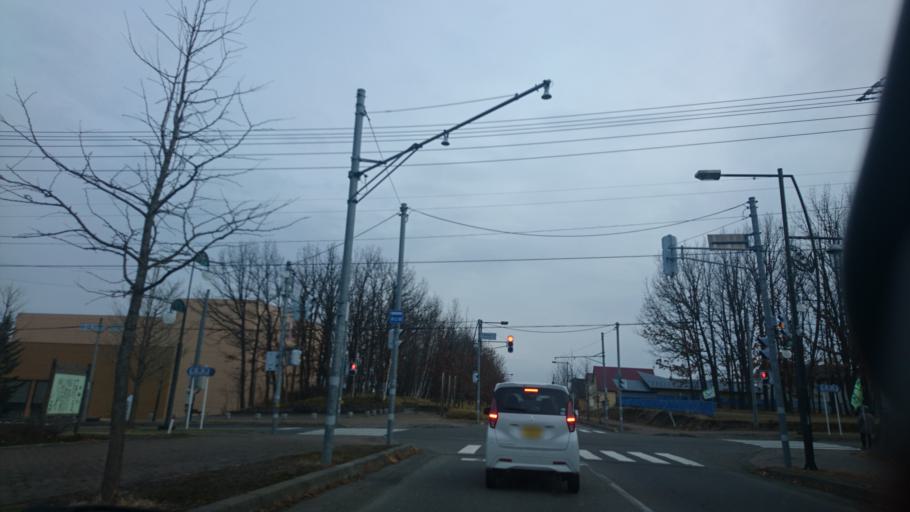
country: JP
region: Hokkaido
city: Otofuke
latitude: 42.9671
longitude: 143.1994
